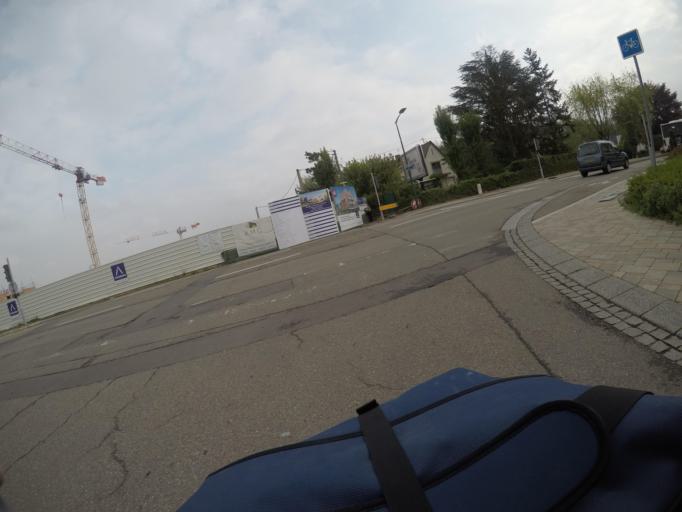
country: FR
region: Alsace
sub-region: Departement du Bas-Rhin
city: Wolfisheim
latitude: 48.5869
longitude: 7.6613
